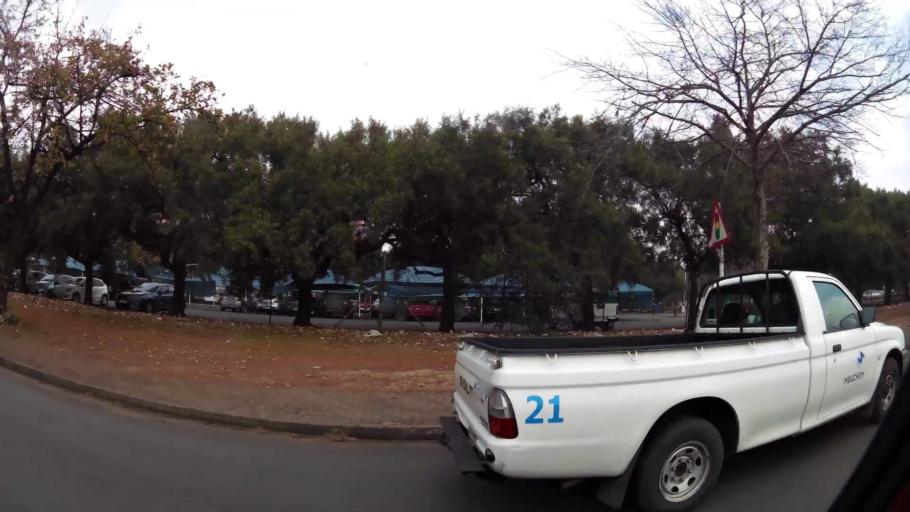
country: ZA
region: Gauteng
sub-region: Sedibeng District Municipality
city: Vanderbijlpark
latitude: -26.7026
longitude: 27.8345
